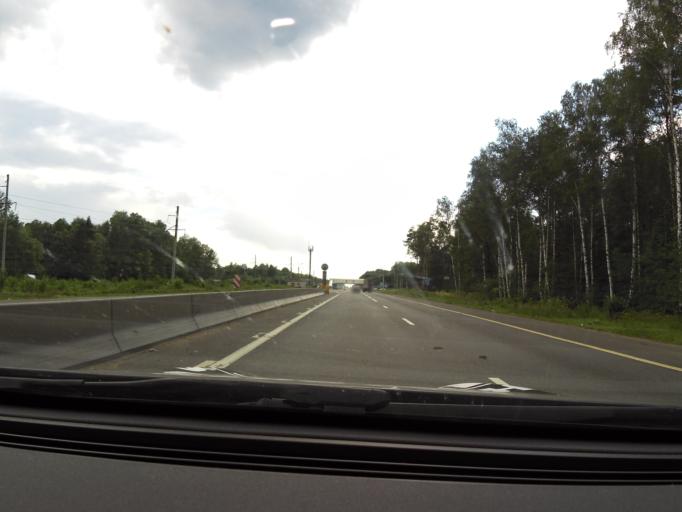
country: RU
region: Nizjnij Novgorod
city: Smolino
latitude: 56.2821
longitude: 43.0990
